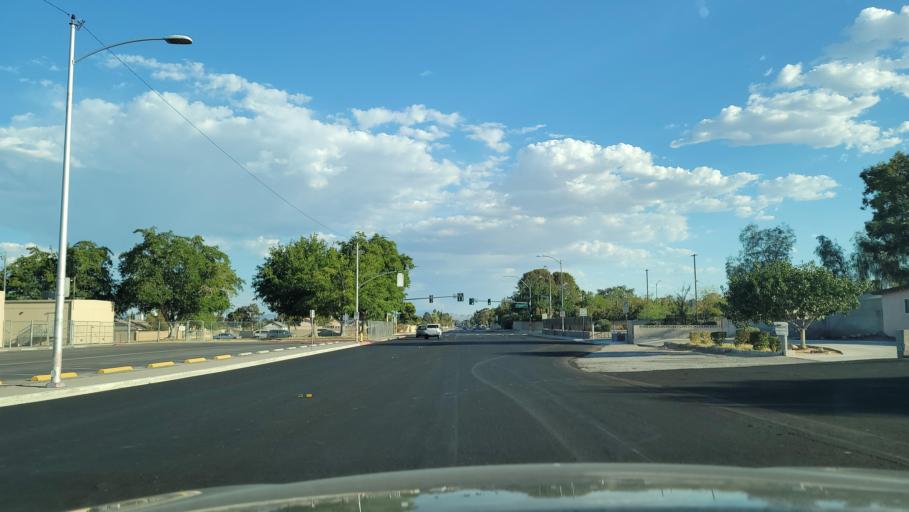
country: US
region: Nevada
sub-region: Clark County
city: Spring Valley
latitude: 36.1530
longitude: -115.2168
